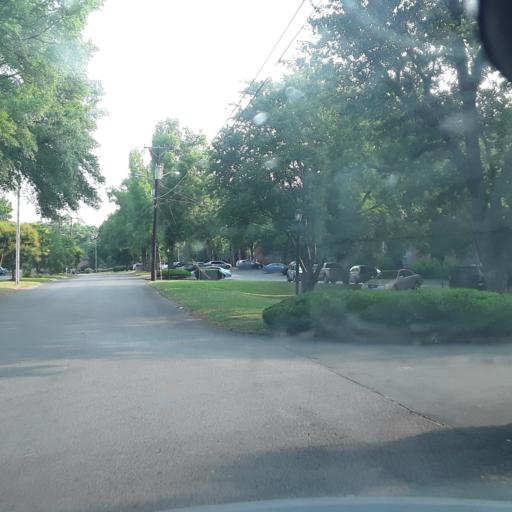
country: US
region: Tennessee
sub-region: Williamson County
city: Brentwood Estates
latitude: 36.0564
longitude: -86.7193
